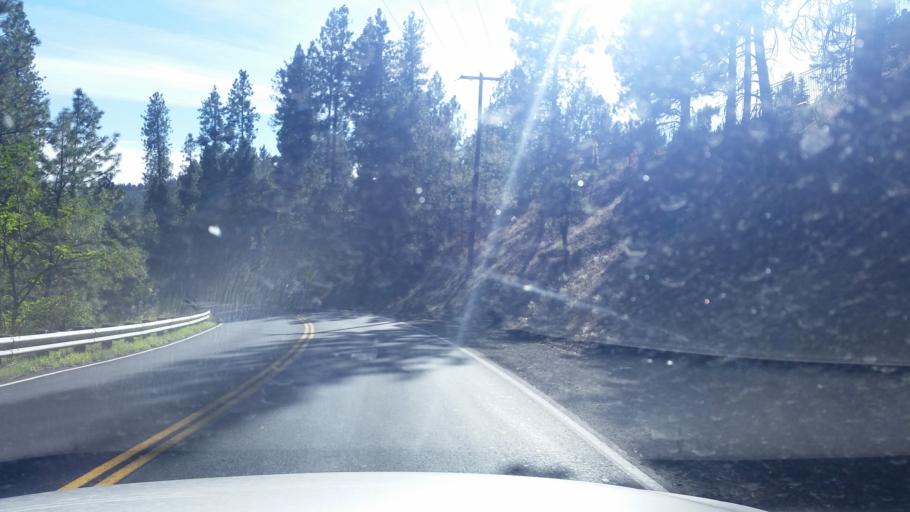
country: US
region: Washington
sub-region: Spokane County
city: Spokane
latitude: 47.5897
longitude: -117.3970
